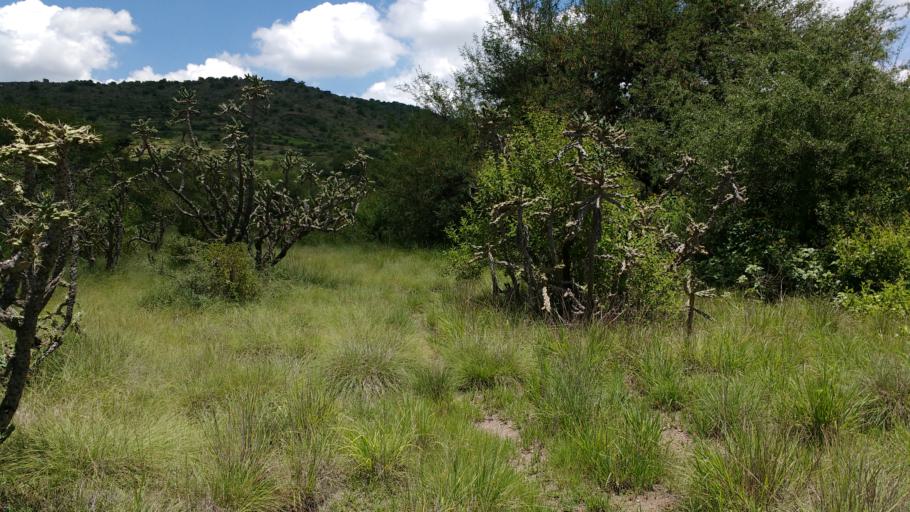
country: MX
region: Hidalgo
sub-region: Tezontepec de Aldama
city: Tenango
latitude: 20.2407
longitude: -99.2755
